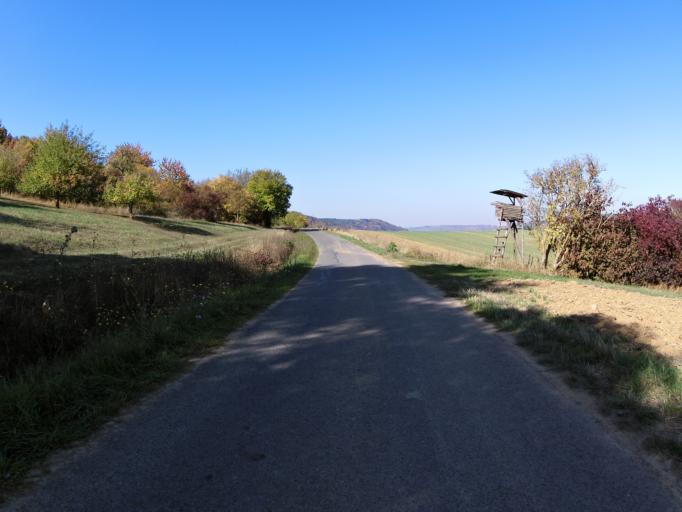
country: DE
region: Bavaria
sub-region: Regierungsbezirk Unterfranken
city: Winterhausen
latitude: 49.7075
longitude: 10.0043
